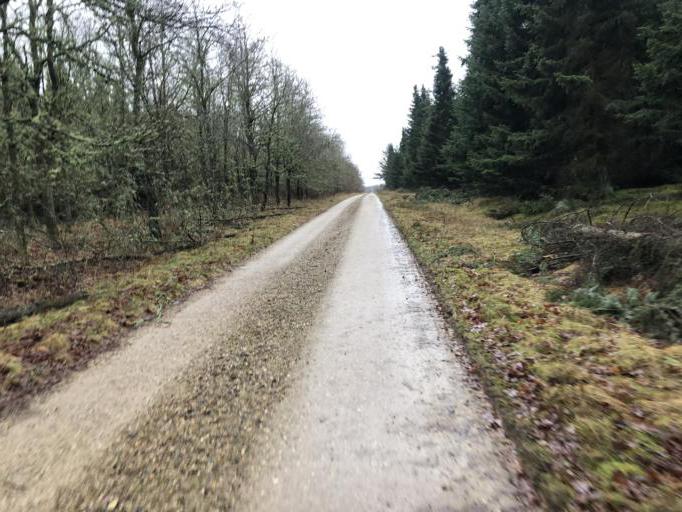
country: DK
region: Central Jutland
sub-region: Holstebro Kommune
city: Ulfborg
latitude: 56.2896
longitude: 8.4574
